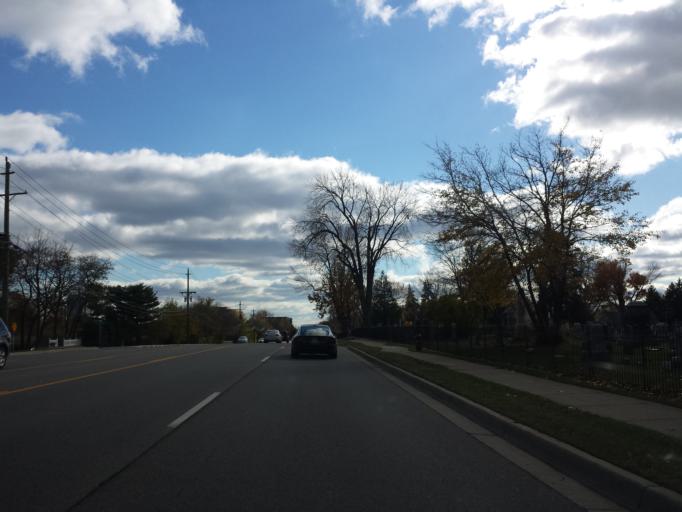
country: US
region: Michigan
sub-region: Oakland County
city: Troy
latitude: 42.5735
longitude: -83.1678
